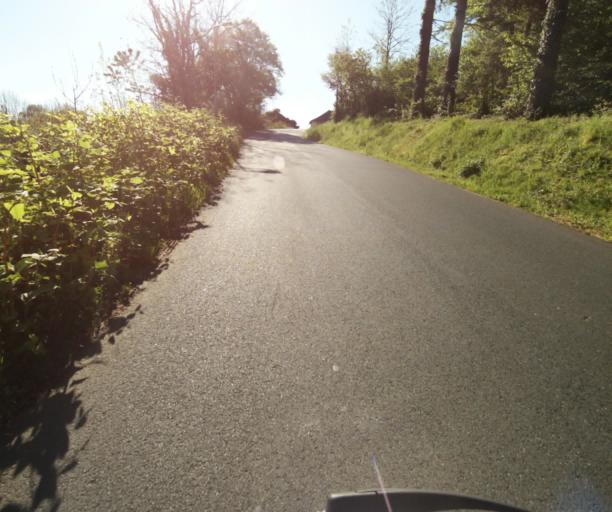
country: FR
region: Limousin
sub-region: Departement de la Correze
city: Tulle
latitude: 45.2719
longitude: 1.7858
